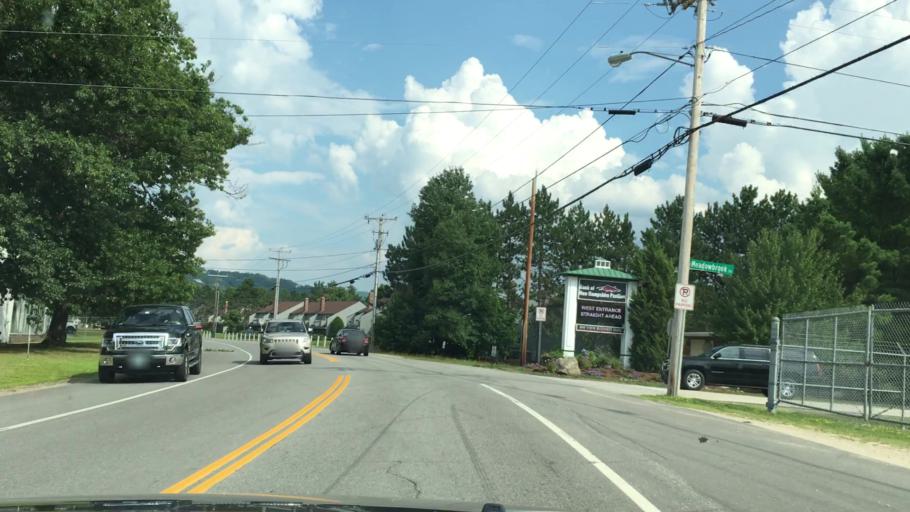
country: US
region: New Hampshire
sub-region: Belknap County
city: Gilford
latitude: 43.5796
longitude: -71.4081
